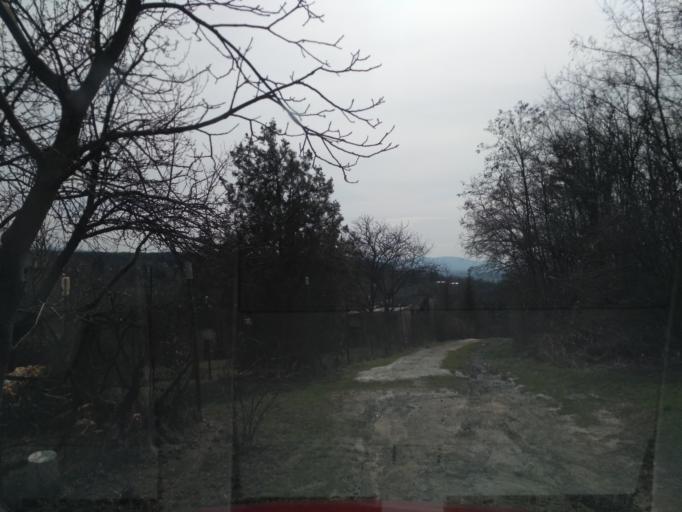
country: SK
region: Kosicky
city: Kosice
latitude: 48.7081
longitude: 21.2882
